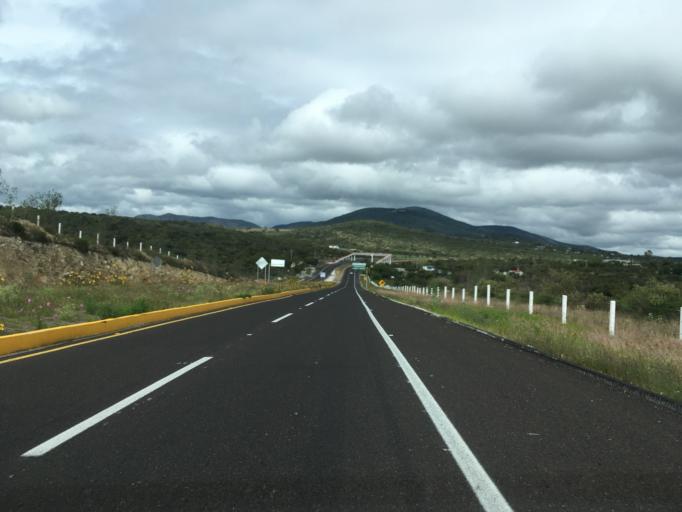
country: MX
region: Hidalgo
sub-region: Atotonilco el Grande
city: Santa Maria Amajac
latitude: 20.3784
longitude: -98.7203
